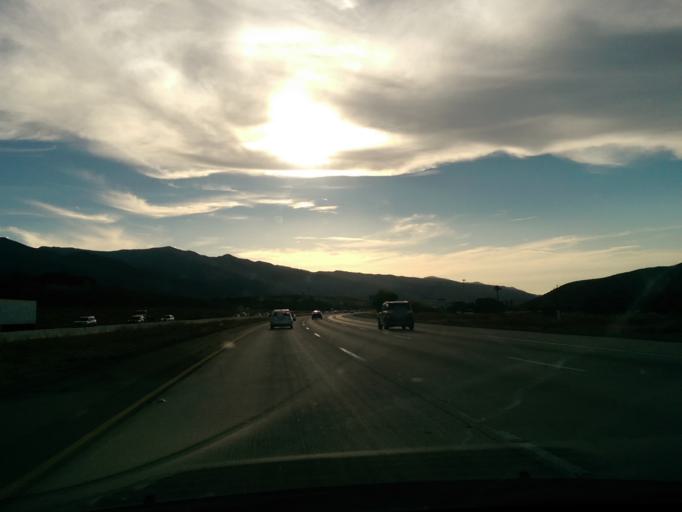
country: US
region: California
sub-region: Riverside County
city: El Cerrito
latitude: 33.7426
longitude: -117.4381
